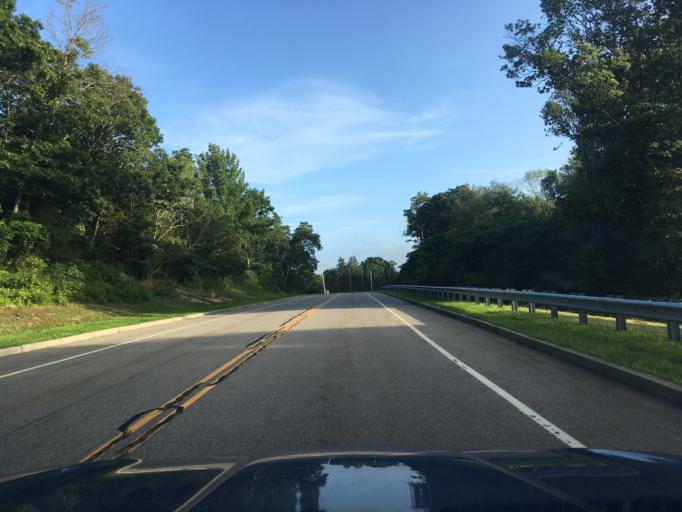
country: US
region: Rhode Island
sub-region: Kent County
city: East Greenwich
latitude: 41.6034
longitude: -71.4257
